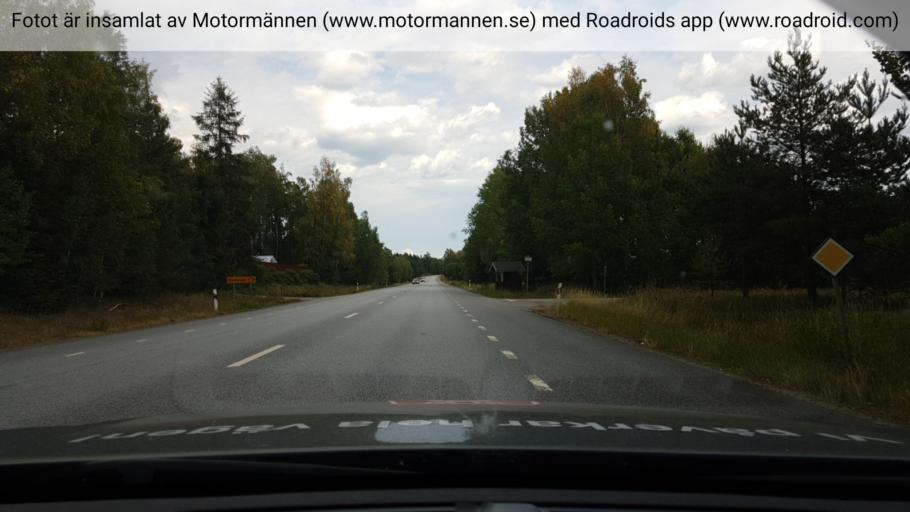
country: SE
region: Uppsala
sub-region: Heby Kommun
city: Morgongava
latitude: 59.8941
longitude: 17.1413
